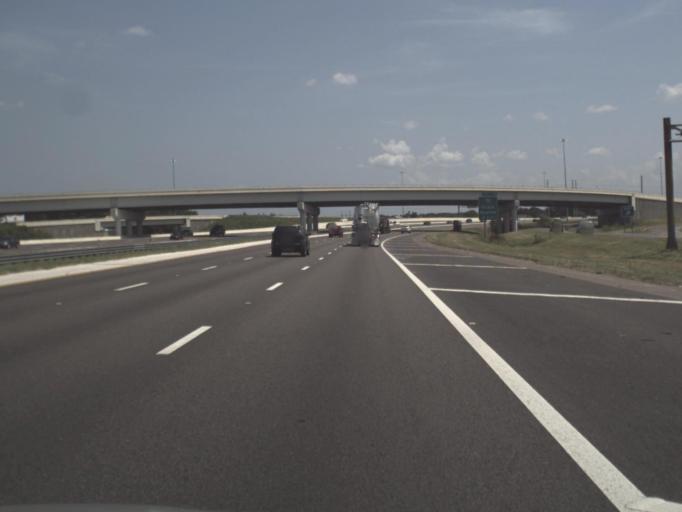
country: US
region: Florida
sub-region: Hillsborough County
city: East Lake-Orient Park
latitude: 27.9937
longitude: -82.3680
